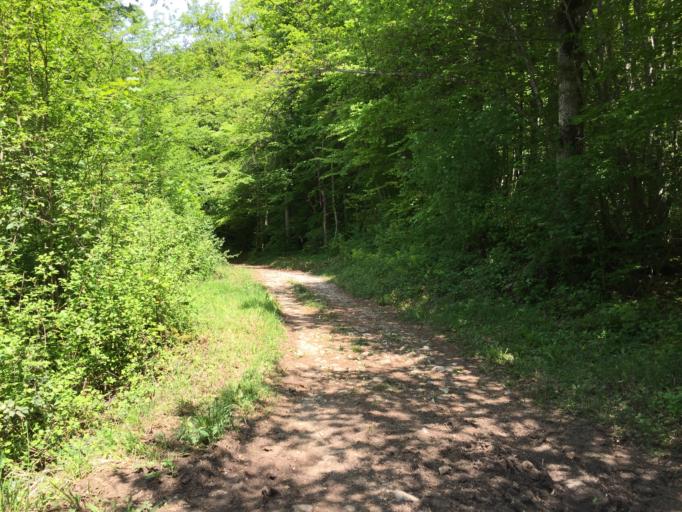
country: FR
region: Rhone-Alpes
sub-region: Departement de la Savoie
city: Mery
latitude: 45.6621
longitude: 5.9506
